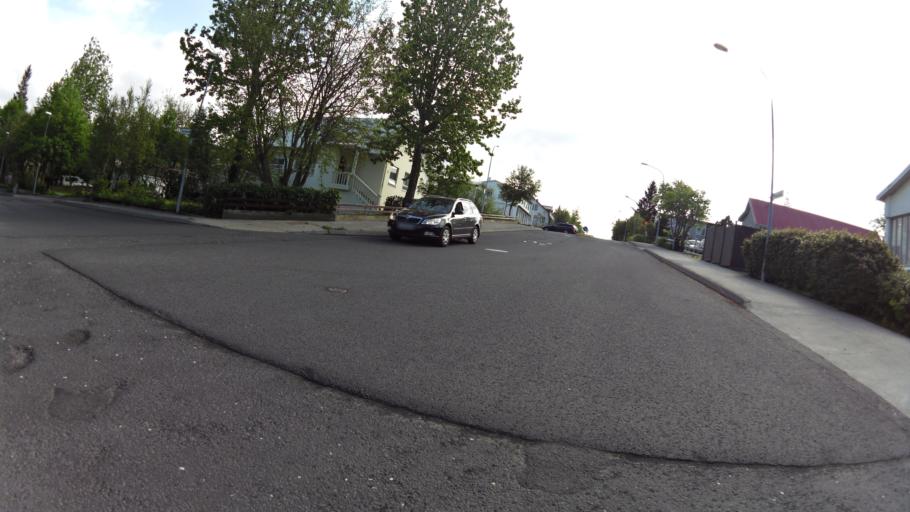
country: IS
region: Capital Region
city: Reykjavik
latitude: 64.1237
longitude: -21.8553
